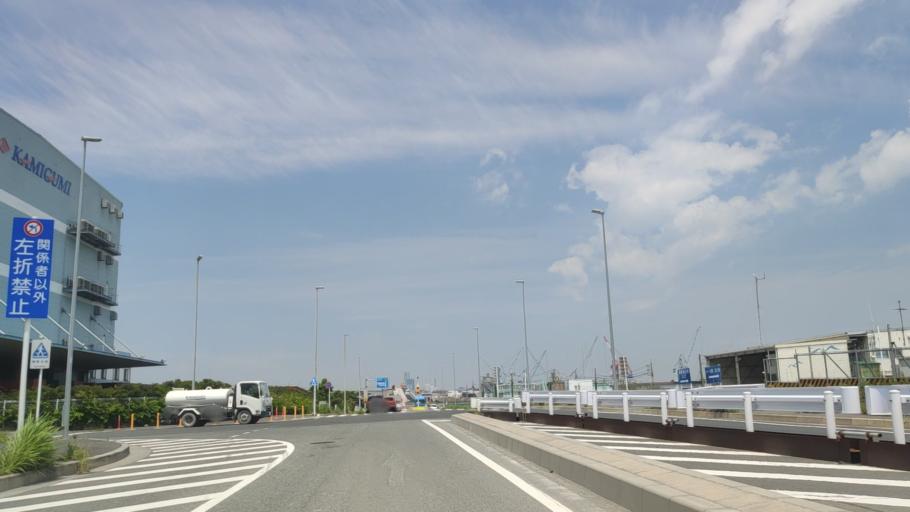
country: JP
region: Kanagawa
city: Yokohama
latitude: 35.4071
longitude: 139.6869
